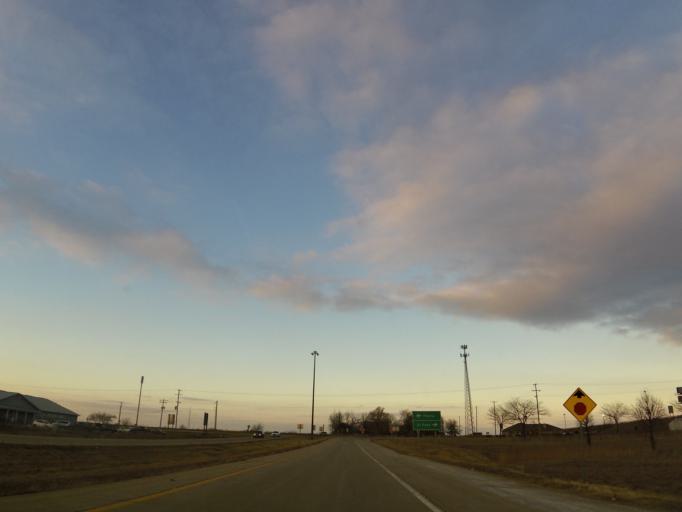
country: US
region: Illinois
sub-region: Woodford County
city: El Paso
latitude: 40.7351
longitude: -89.0371
